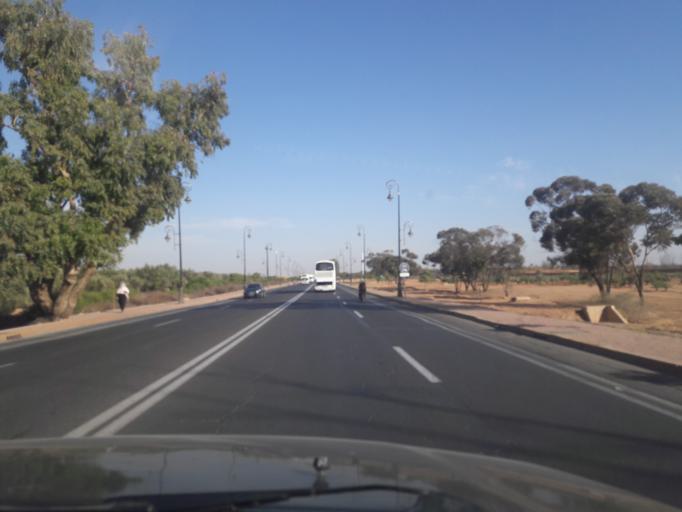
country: MA
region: Marrakech-Tensift-Al Haouz
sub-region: Marrakech
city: Marrakesh
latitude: 31.6479
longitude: -7.9345
